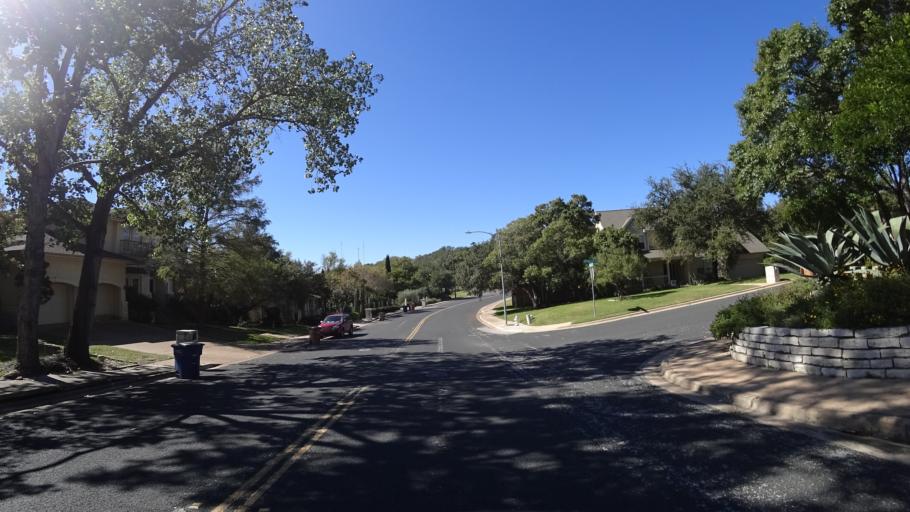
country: US
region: Texas
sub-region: Travis County
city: West Lake Hills
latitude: 30.3439
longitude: -97.7766
